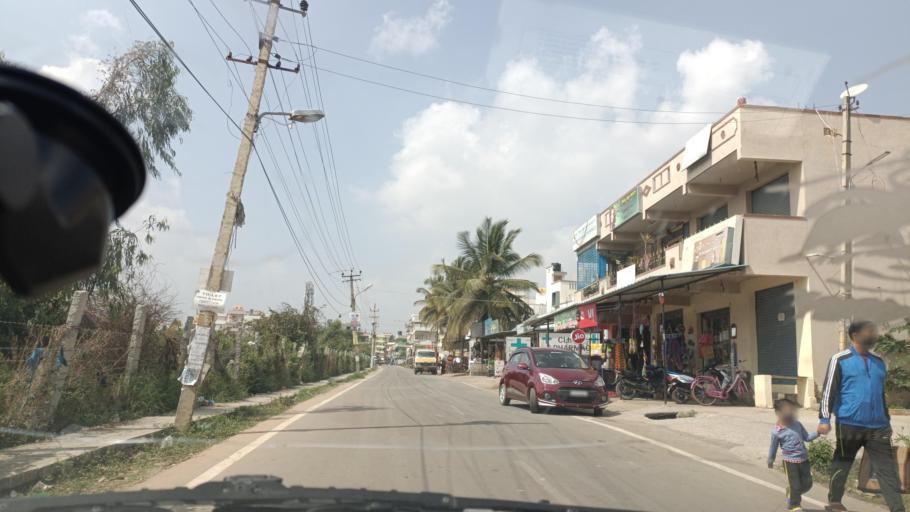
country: IN
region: Karnataka
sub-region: Bangalore Urban
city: Yelahanka
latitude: 13.1430
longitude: 77.6233
